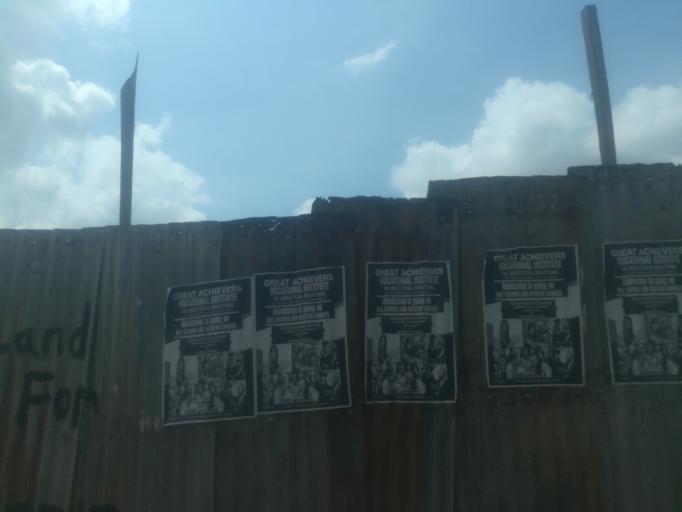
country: NG
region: Oyo
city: Ibadan
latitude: 7.3648
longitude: 3.8783
